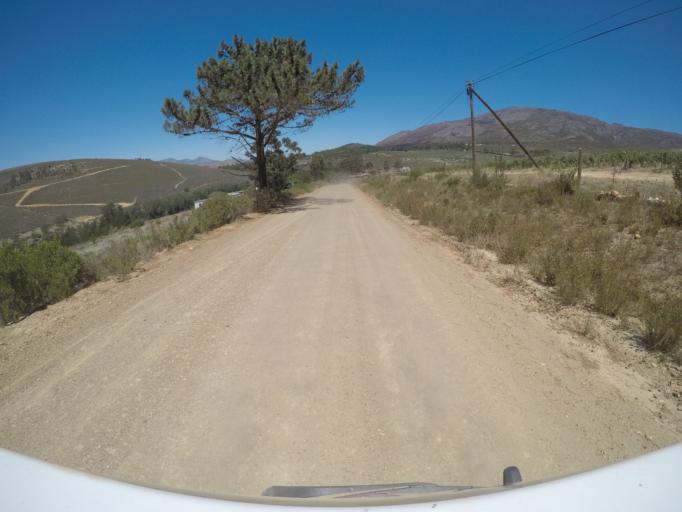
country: ZA
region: Western Cape
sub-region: Overberg District Municipality
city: Caledon
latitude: -34.1776
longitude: 19.2255
